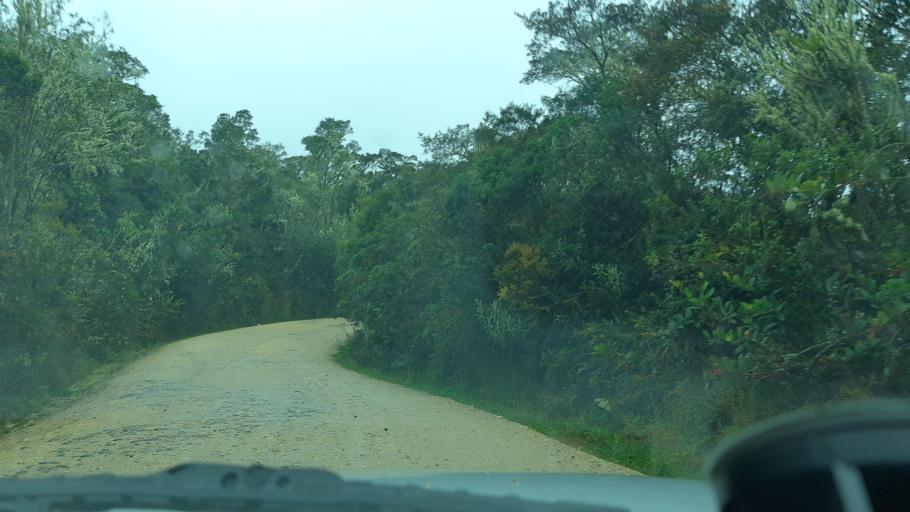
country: CO
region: Cundinamarca
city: Villapinzon
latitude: 5.2161
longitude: -73.5393
